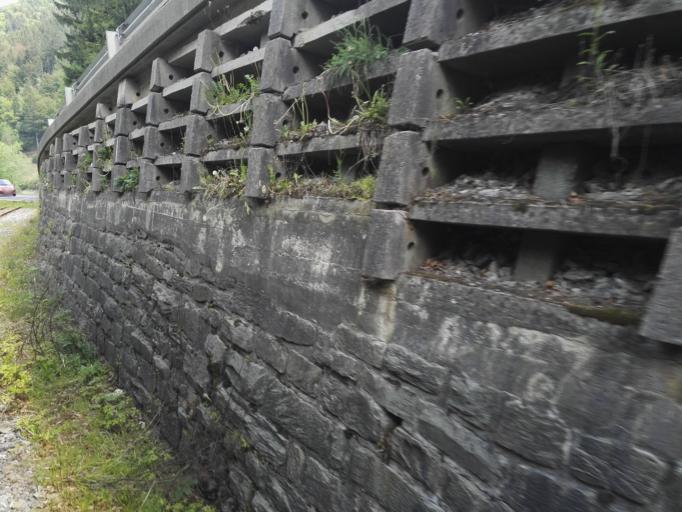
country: AT
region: Styria
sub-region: Politischer Bezirk Weiz
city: Koglhof
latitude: 47.3045
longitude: 15.6938
